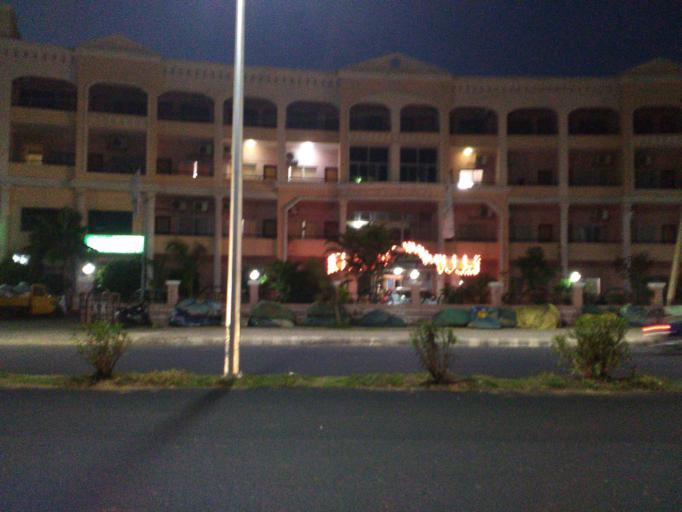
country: IN
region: Andhra Pradesh
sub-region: Vishakhapatnam
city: Yarada
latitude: 17.7413
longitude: 83.3436
